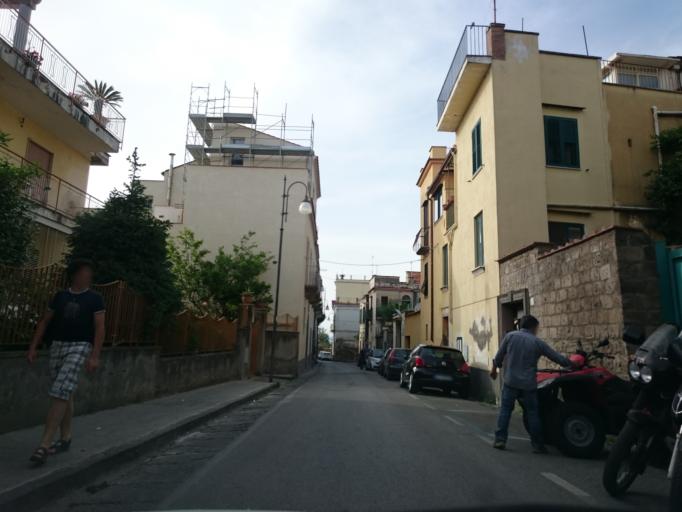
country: IT
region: Campania
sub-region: Provincia di Napoli
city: Sant'Agnello
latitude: 40.6339
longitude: 14.4008
